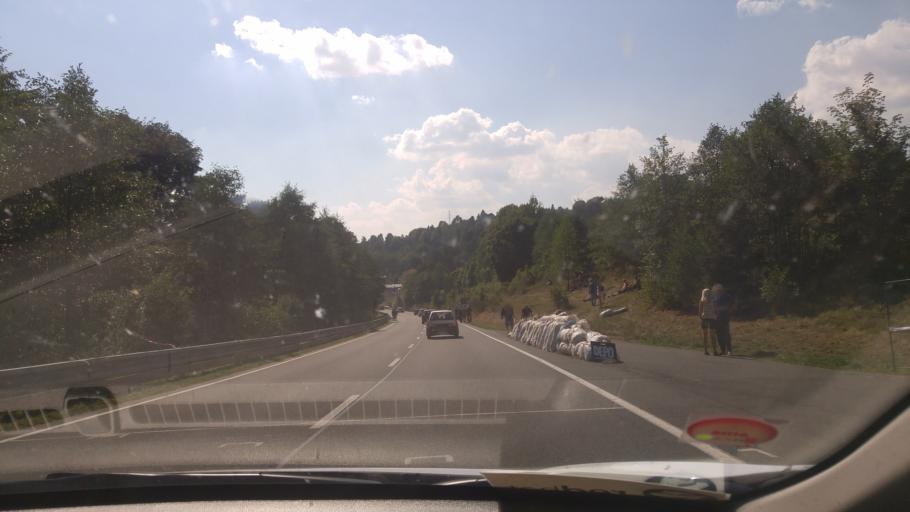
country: CZ
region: Olomoucky
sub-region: Okres Sumperk
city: Stare Mesto
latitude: 50.1562
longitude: 17.0122
